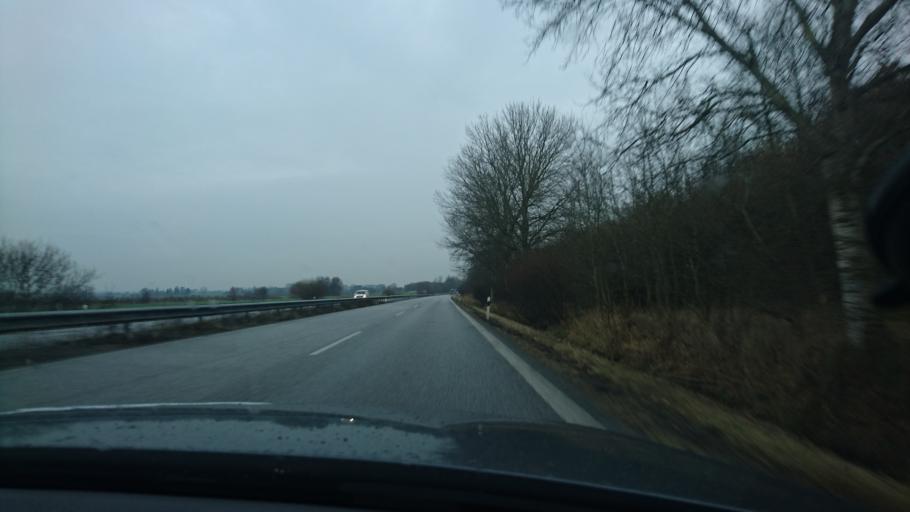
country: DE
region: Schleswig-Holstein
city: Altenkrempe
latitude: 54.1432
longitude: 10.8444
